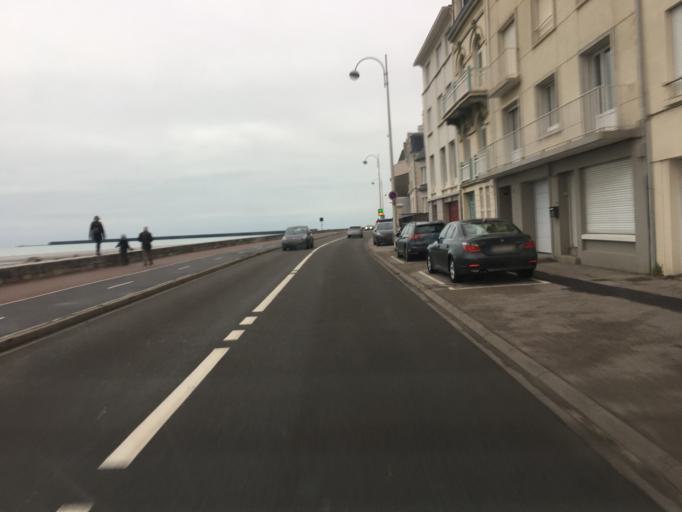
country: FR
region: Nord-Pas-de-Calais
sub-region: Departement du Pas-de-Calais
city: Saint-Martin-Boulogne
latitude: 50.7355
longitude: 1.5945
